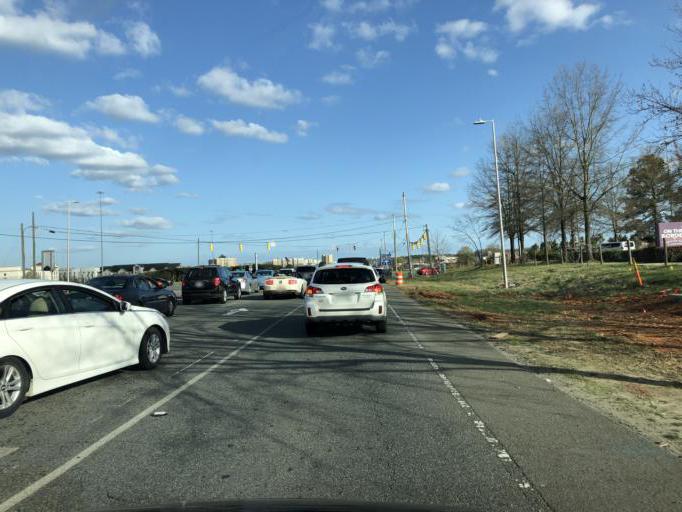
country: US
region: North Carolina
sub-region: Cabarrus County
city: Harrisburg
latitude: 35.3700
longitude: -80.7160
